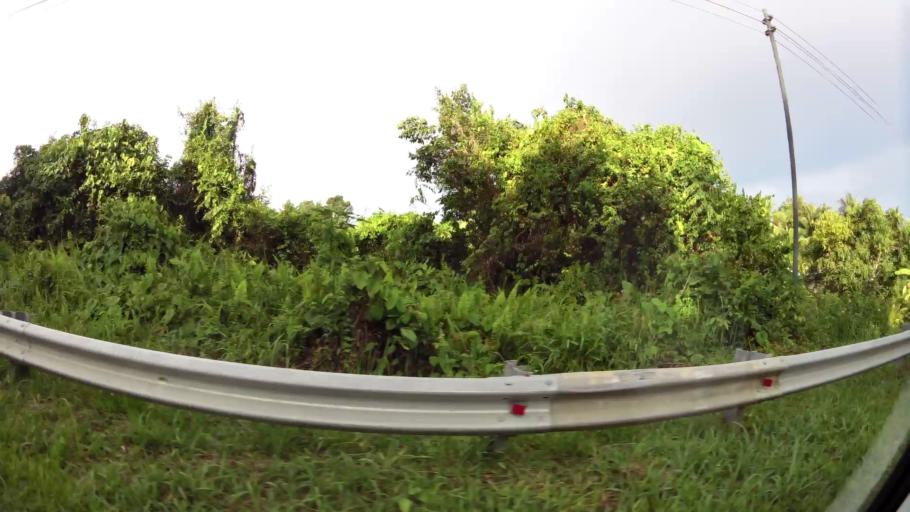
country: BN
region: Brunei and Muara
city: Bandar Seri Begawan
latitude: 4.9588
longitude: 115.0197
